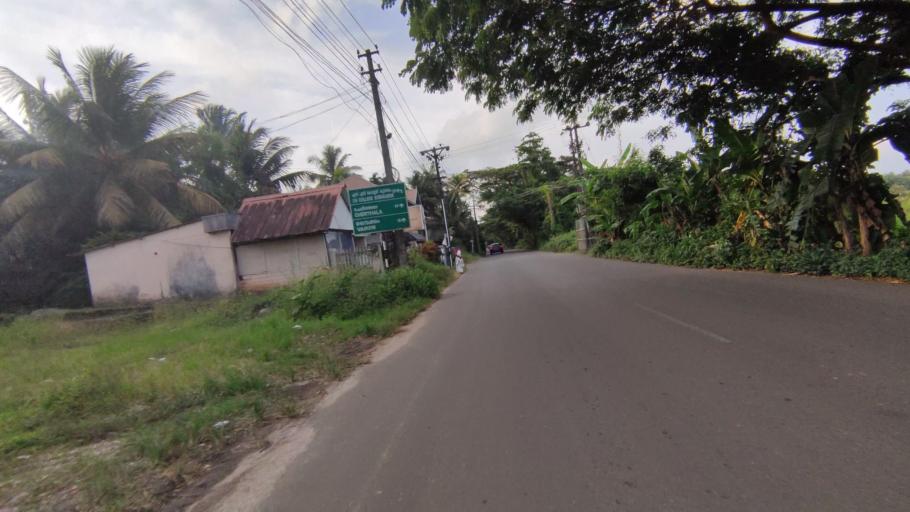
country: IN
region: Kerala
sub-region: Kottayam
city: Kottayam
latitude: 9.6120
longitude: 76.4335
